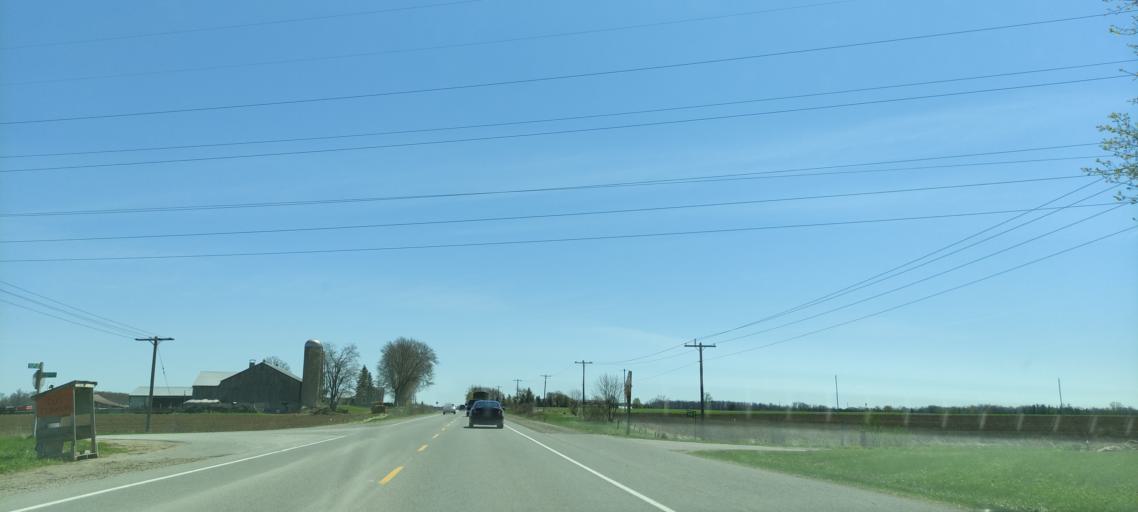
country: CA
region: Ontario
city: Waterloo
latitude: 43.5840
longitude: -80.4424
